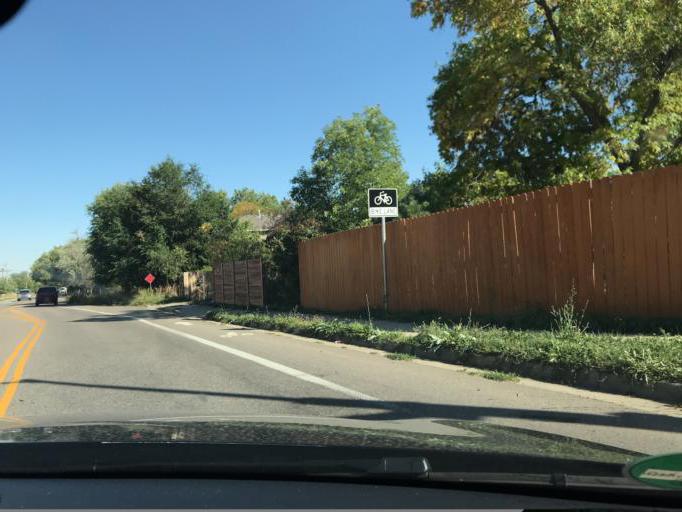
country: US
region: Colorado
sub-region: Boulder County
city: Boulder
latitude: 40.0546
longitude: -105.2820
